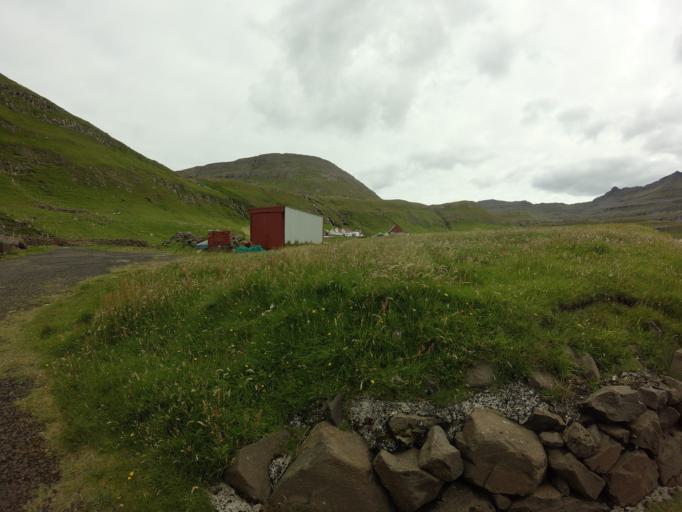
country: FO
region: Suduroy
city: Tvoroyri
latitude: 61.5264
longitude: -6.8857
